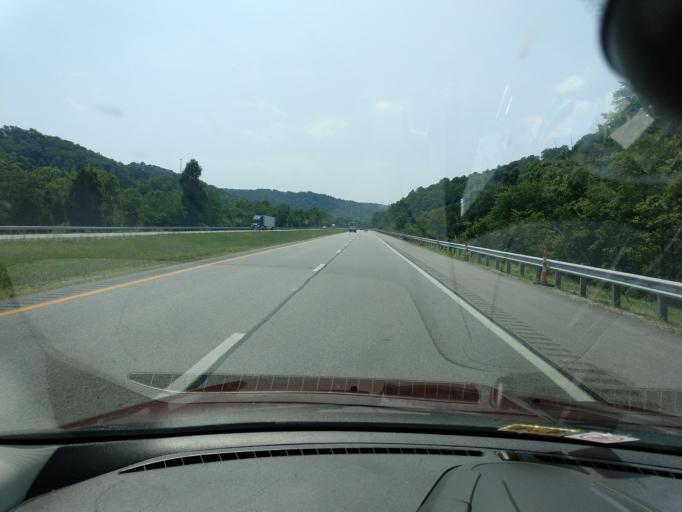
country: US
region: West Virginia
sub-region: Jackson County
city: Ripley
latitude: 38.7188
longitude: -81.6482
